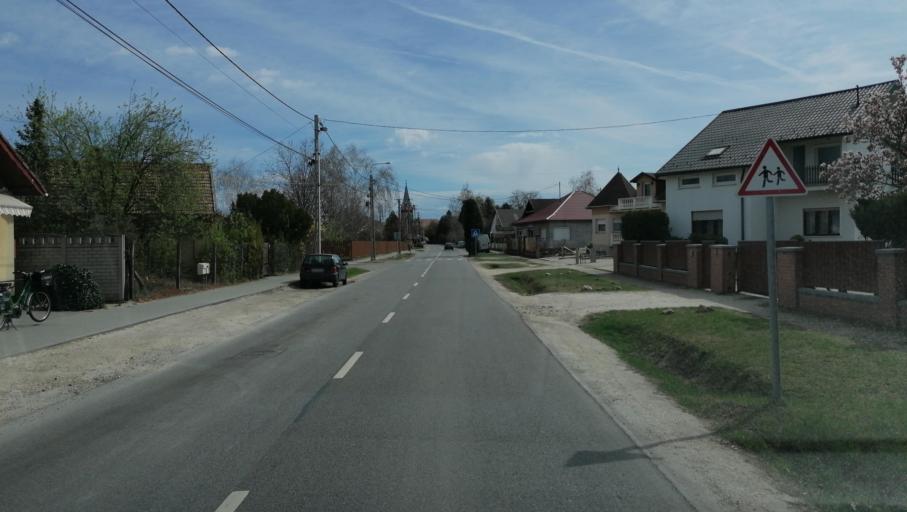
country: HU
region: Pest
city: Dabas
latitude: 47.1718
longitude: 19.3271
